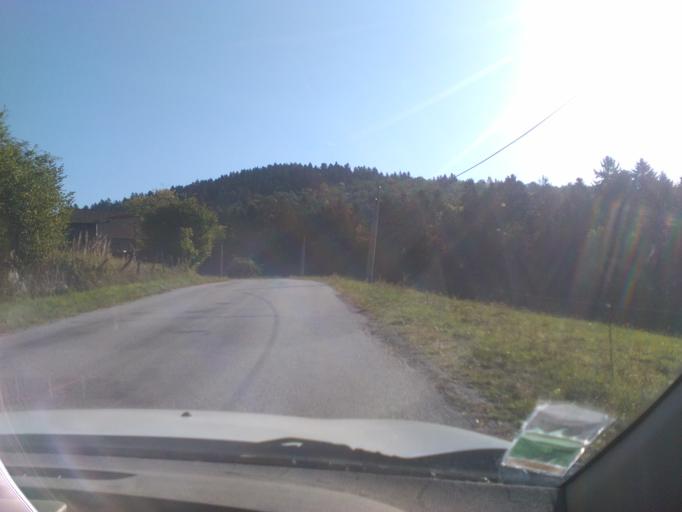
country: FR
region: Lorraine
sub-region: Departement des Vosges
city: Vagney
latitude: 48.0336
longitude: 6.7328
